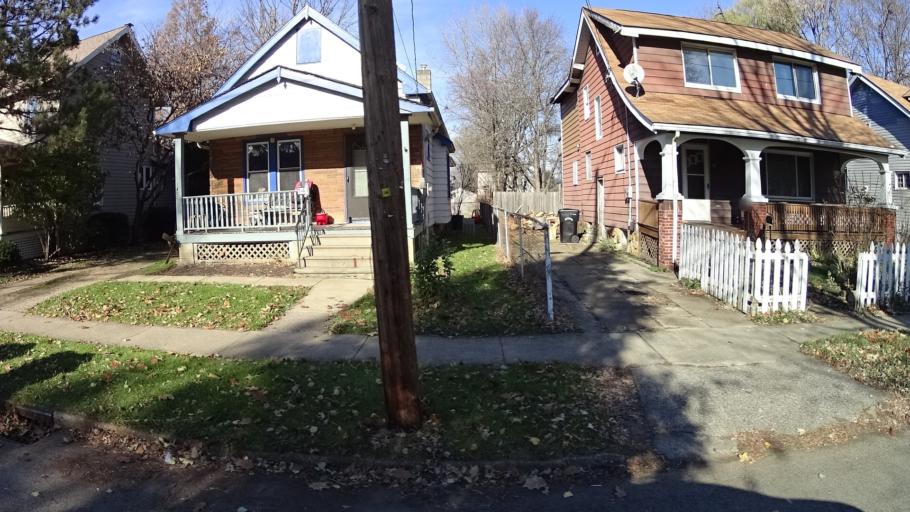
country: US
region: Ohio
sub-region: Lorain County
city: Elyria
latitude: 41.3760
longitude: -82.1153
